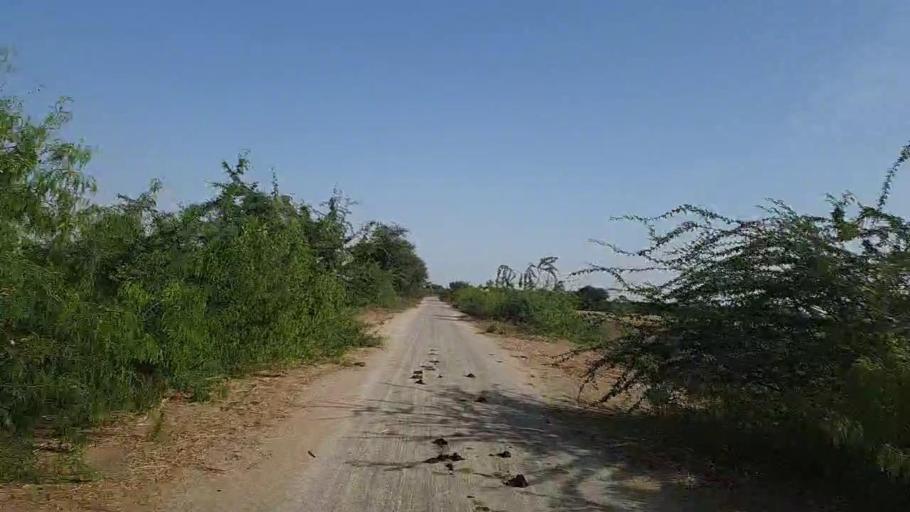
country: PK
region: Sindh
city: Kotri
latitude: 25.1479
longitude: 68.2949
